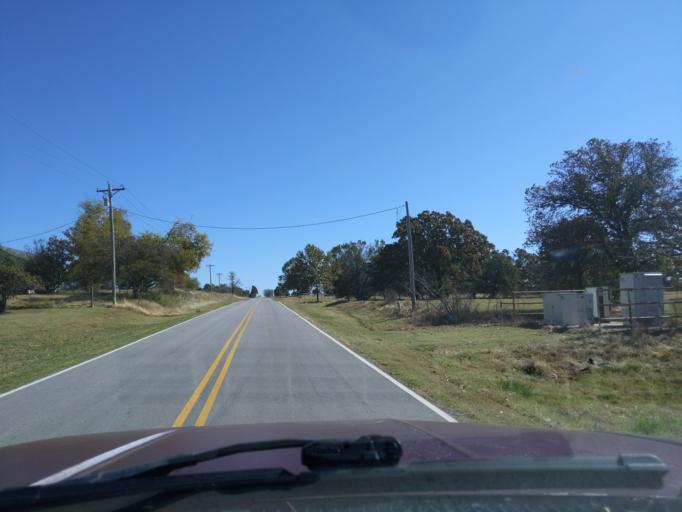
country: US
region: Oklahoma
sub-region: Creek County
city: Bristow
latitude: 35.7120
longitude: -96.4053
